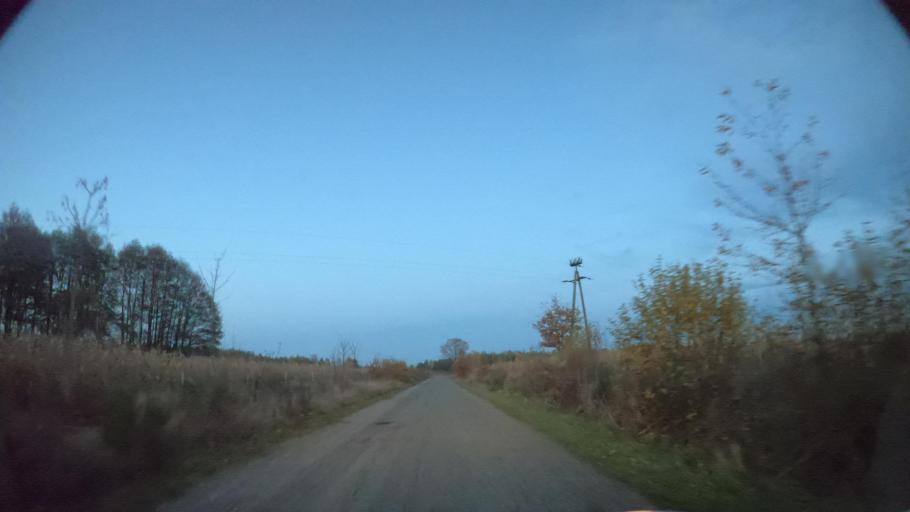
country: PL
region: Greater Poland Voivodeship
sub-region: Powiat zlotowski
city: Sypniewo
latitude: 53.4259
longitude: 16.6437
